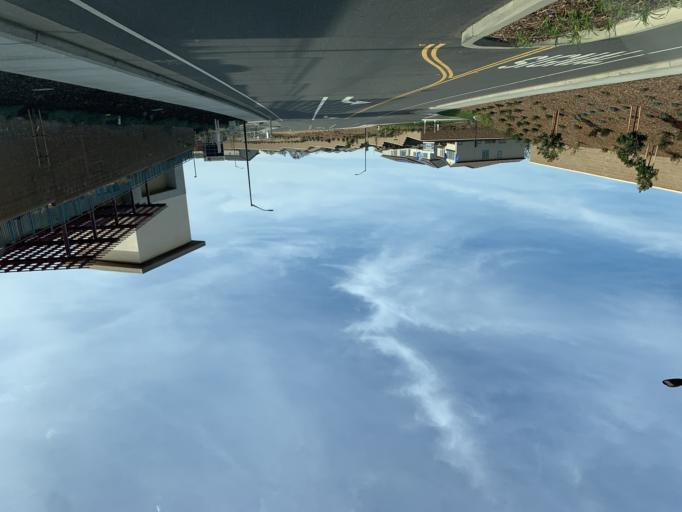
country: US
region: California
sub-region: El Dorado County
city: Cameron Park
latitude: 38.6761
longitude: -121.0281
